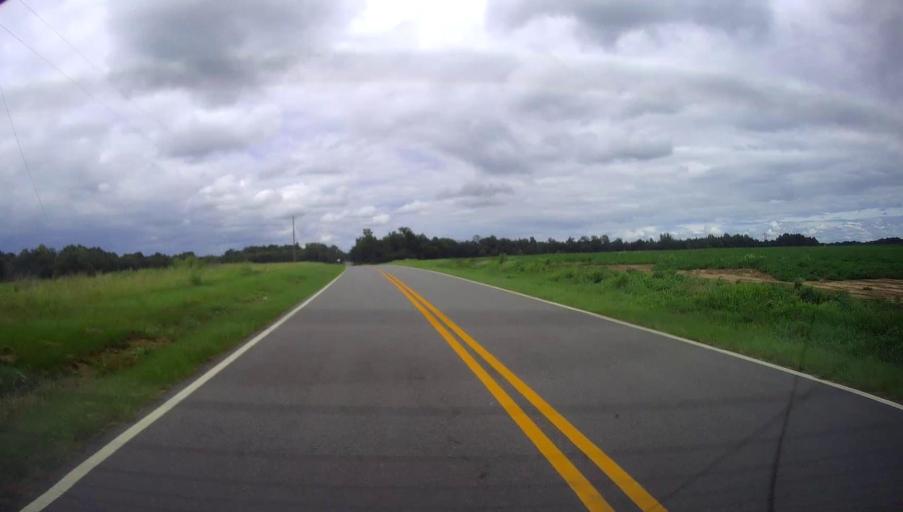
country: US
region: Georgia
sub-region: Bleckley County
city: Cochran
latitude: 32.5225
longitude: -83.3672
